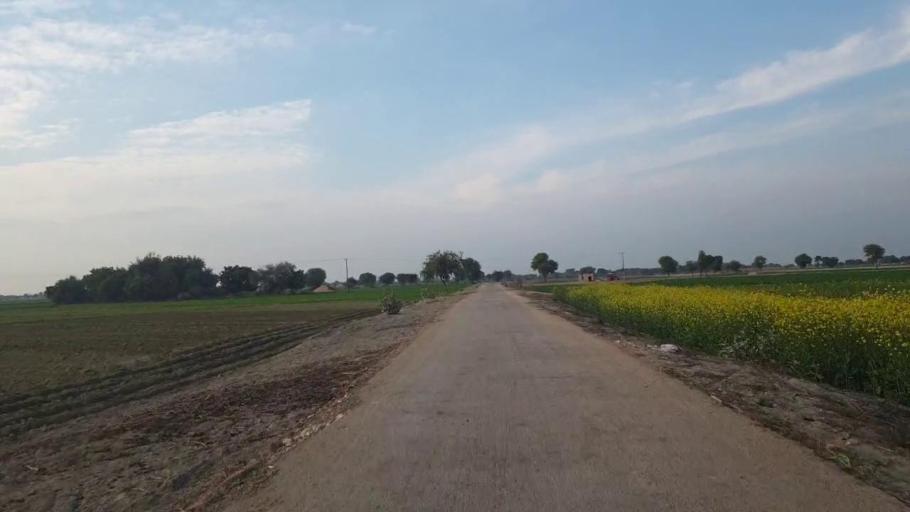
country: PK
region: Sindh
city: Shahpur Chakar
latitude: 26.1001
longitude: 68.5480
